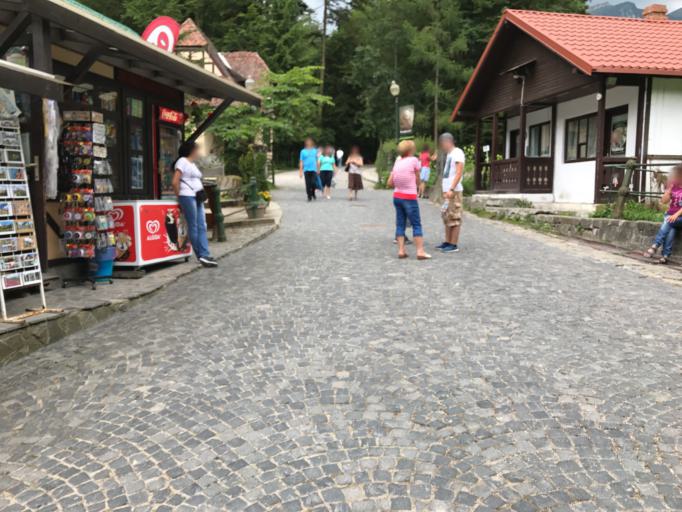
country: RO
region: Prahova
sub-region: Oras Sinaia
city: Sinaia
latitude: 45.3588
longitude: 25.5441
